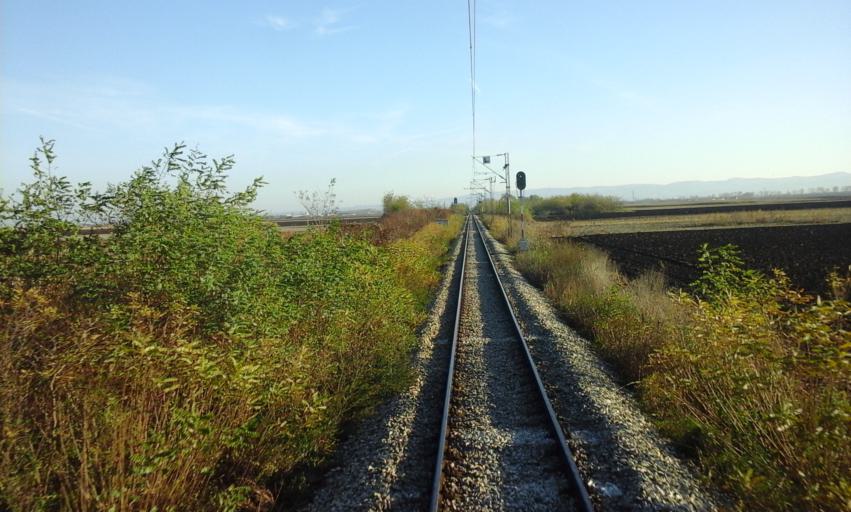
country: RS
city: Rumenka
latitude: 45.3192
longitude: 19.7637
